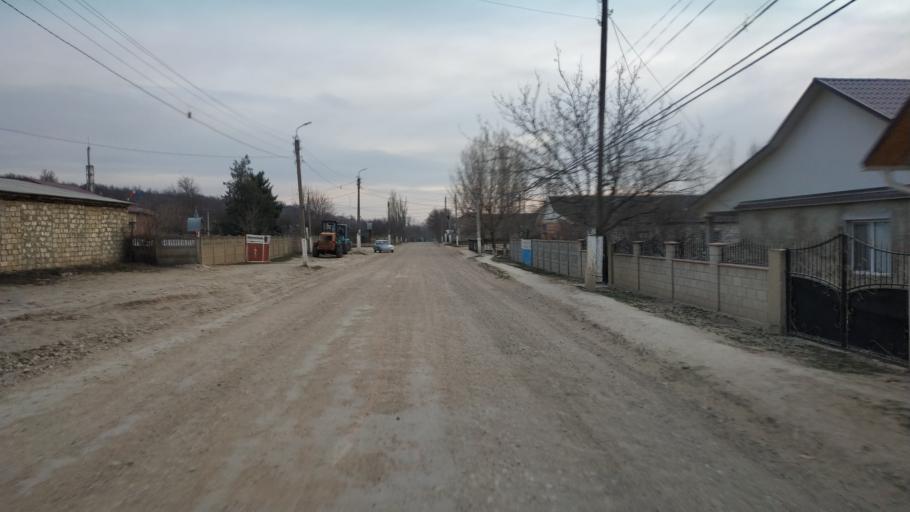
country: MD
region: Hincesti
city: Dancu
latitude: 46.7568
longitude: 28.2083
